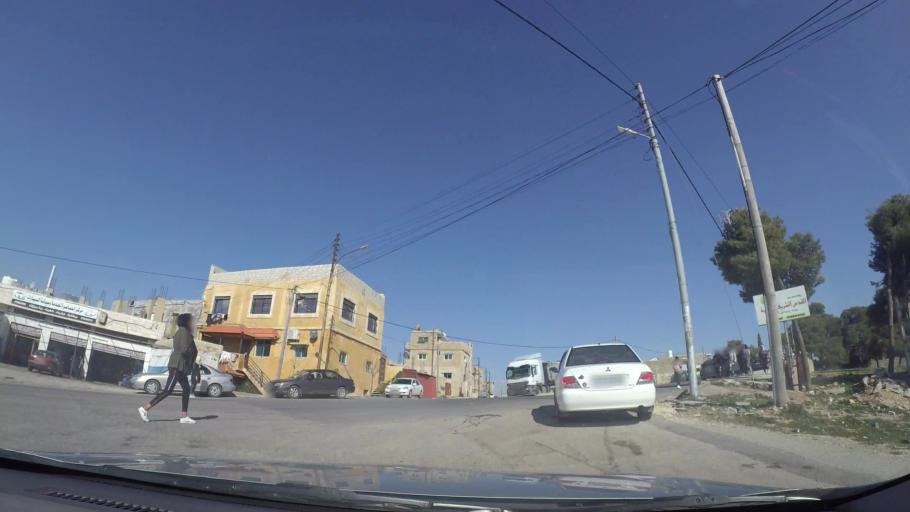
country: JO
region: Amman
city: Al Bunayyat ash Shamaliyah
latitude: 31.9094
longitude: 35.8934
